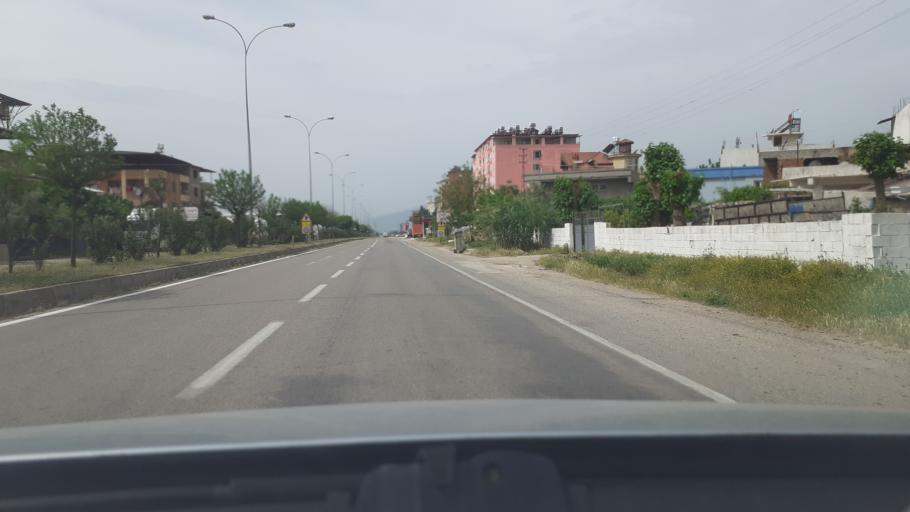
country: TR
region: Hatay
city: Kirikhan
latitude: 36.4830
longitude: 36.3603
